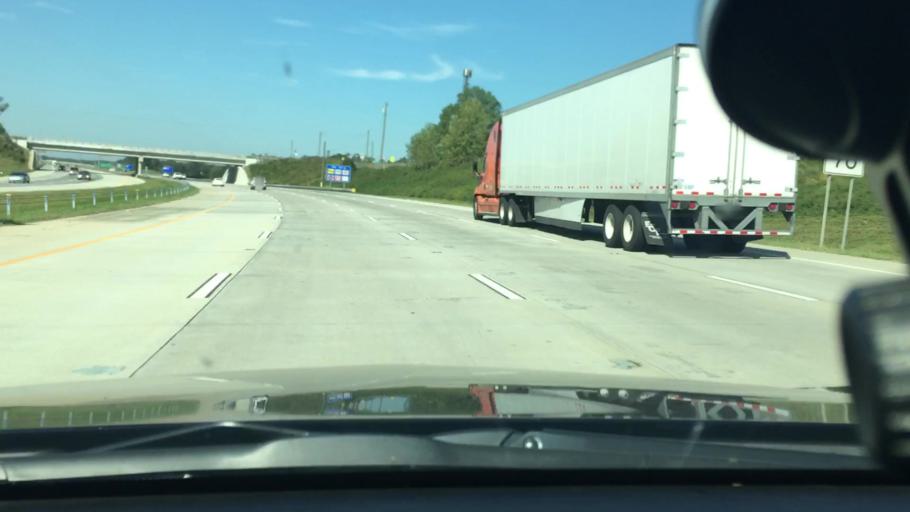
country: US
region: North Carolina
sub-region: Mecklenburg County
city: Huntersville
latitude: 35.3681
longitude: -80.7653
